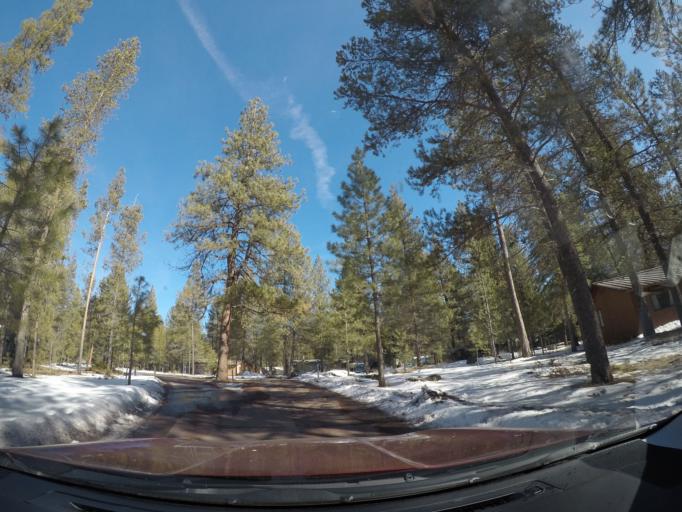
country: US
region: Oregon
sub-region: Deschutes County
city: Sunriver
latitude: 43.8777
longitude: -121.4300
